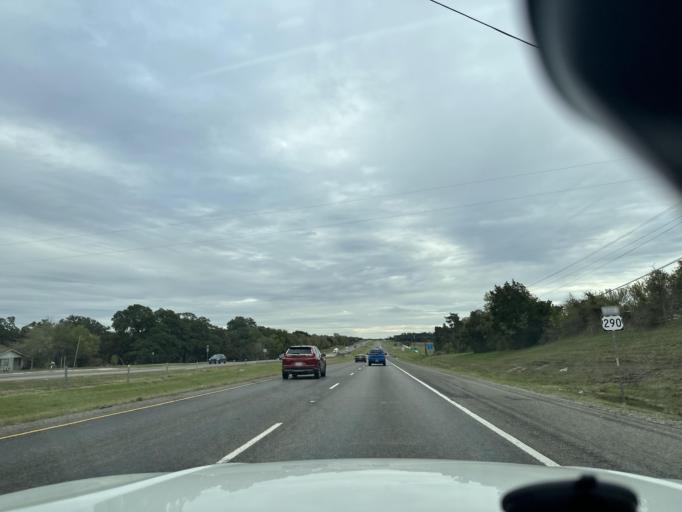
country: US
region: Texas
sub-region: Washington County
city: Brenham
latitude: 30.1893
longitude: -96.5496
